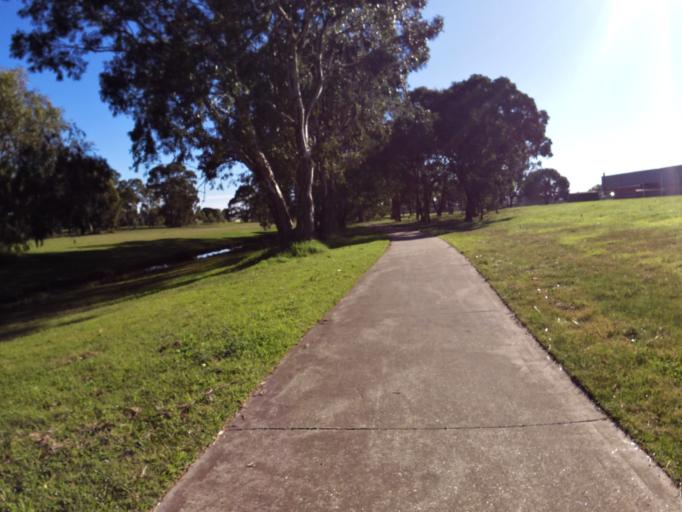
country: AU
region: Victoria
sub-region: Wyndham
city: Tarneit
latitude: -37.8818
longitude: 144.6788
